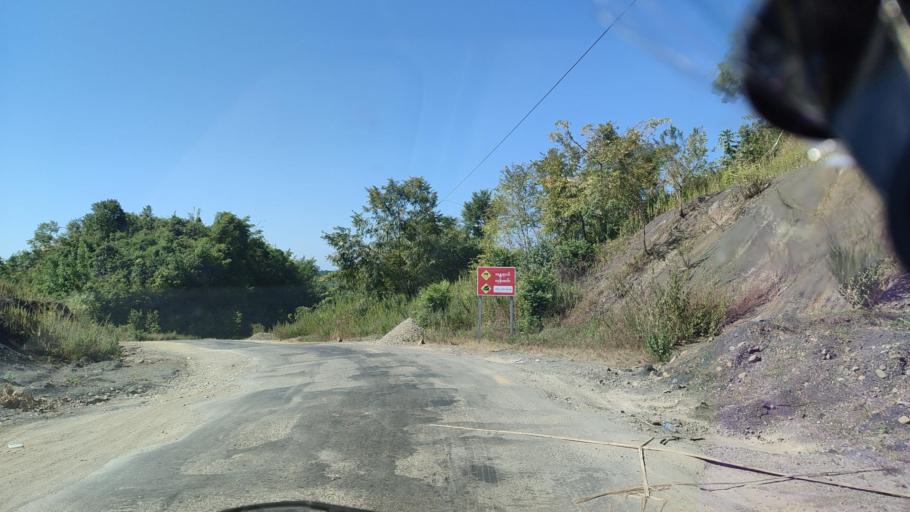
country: MM
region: Rakhine
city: Sittwe
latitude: 19.9814
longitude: 93.6327
